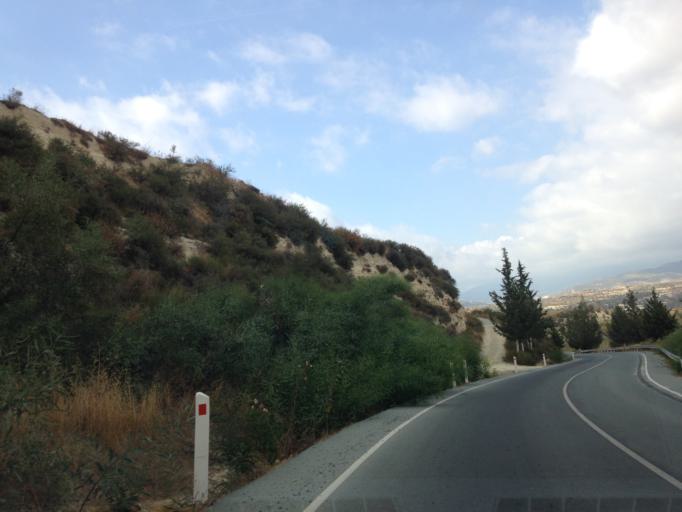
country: CY
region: Limassol
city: Pachna
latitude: 34.7856
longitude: 32.7967
